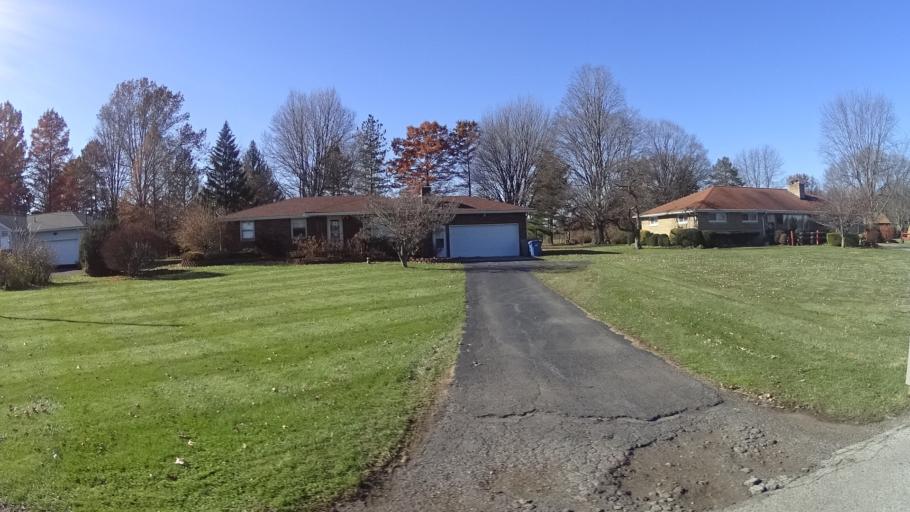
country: US
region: Ohio
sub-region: Lorain County
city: Elyria
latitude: 41.3608
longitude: -82.1579
